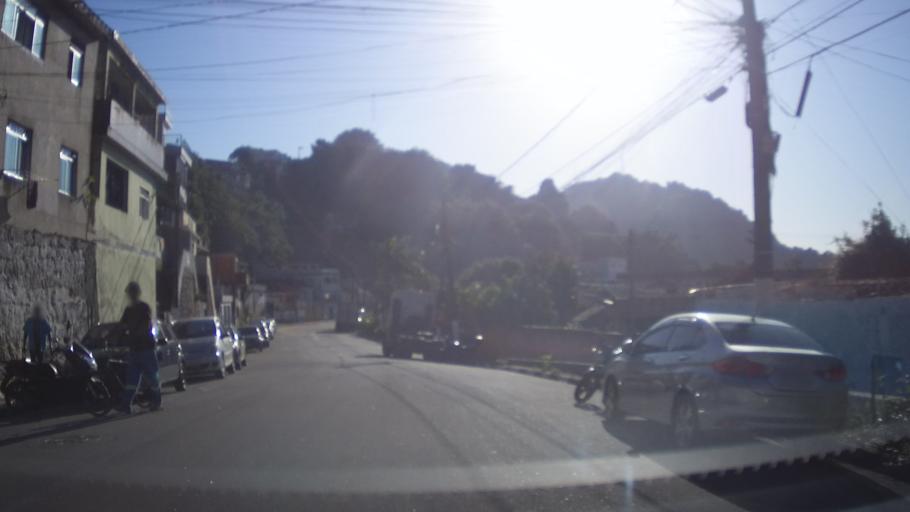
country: BR
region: Sao Paulo
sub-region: Santos
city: Santos
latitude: -23.9404
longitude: -46.3415
